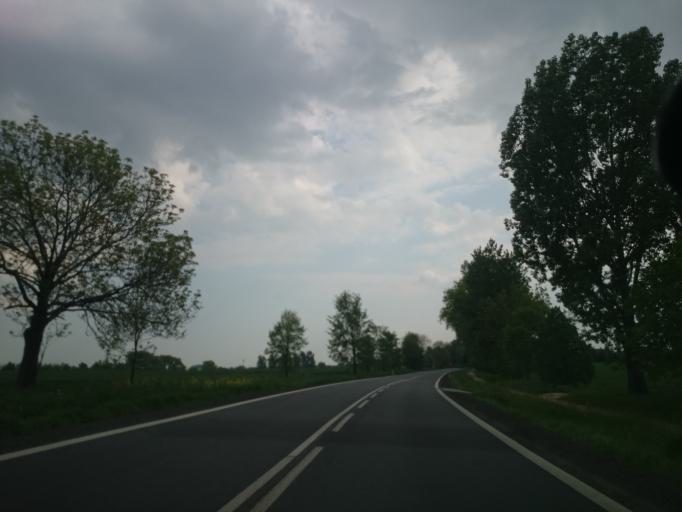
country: PL
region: Lower Silesian Voivodeship
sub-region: Powiat dzierzoniowski
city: Niemcza
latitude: 50.7013
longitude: 16.8230
